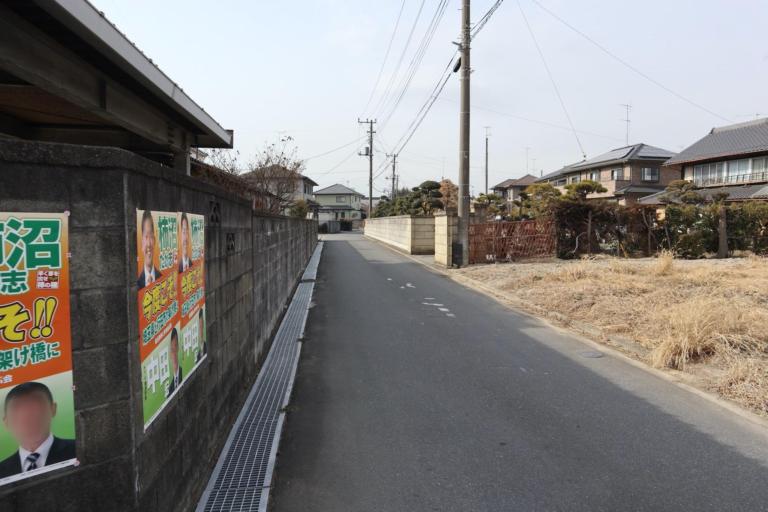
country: JP
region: Saitama
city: Gyoda
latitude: 36.1497
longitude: 139.4691
